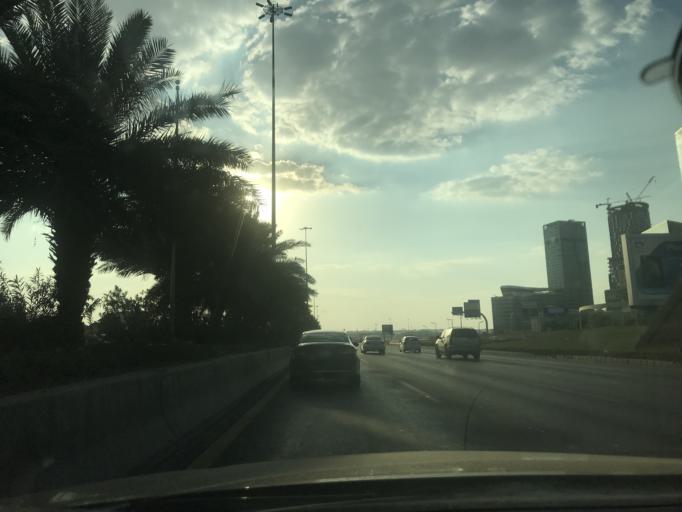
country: SA
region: Ar Riyad
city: Riyadh
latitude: 24.7600
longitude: 46.6444
